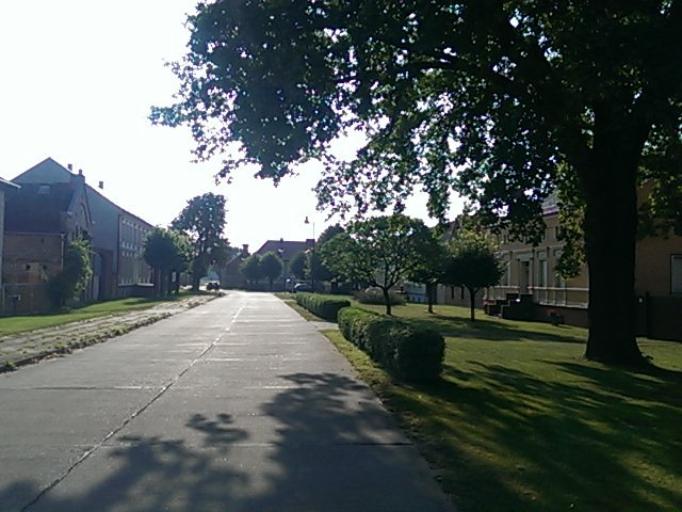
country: DE
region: Brandenburg
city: Michendorf
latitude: 52.2698
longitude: 13.1206
